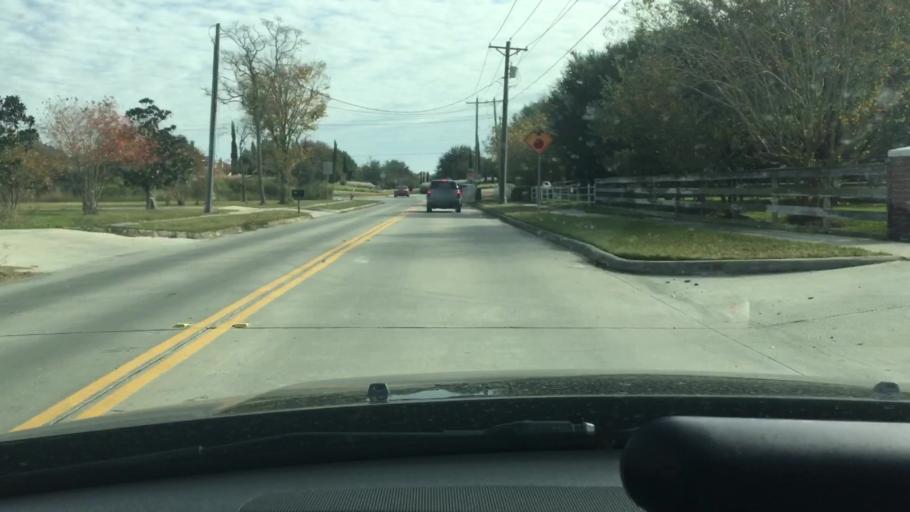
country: US
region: Texas
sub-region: Galveston County
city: League City
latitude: 29.5058
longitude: -95.0609
